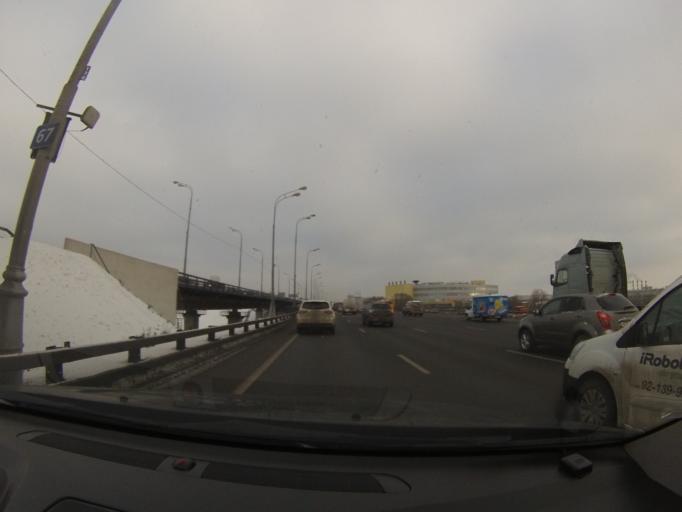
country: RU
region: Moscow
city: Strogino
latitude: 55.8280
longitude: 37.3943
